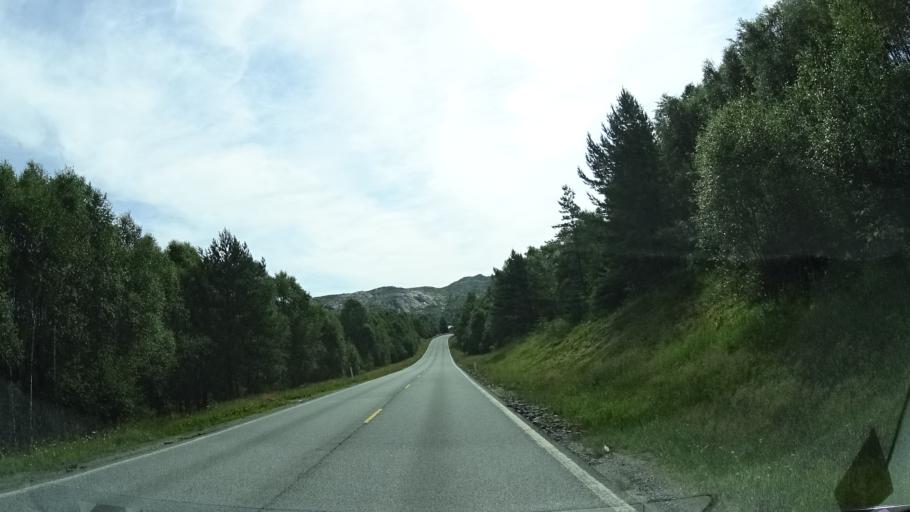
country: NO
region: Rogaland
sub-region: Tysvaer
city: Aksdal
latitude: 59.4854
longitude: 5.4500
